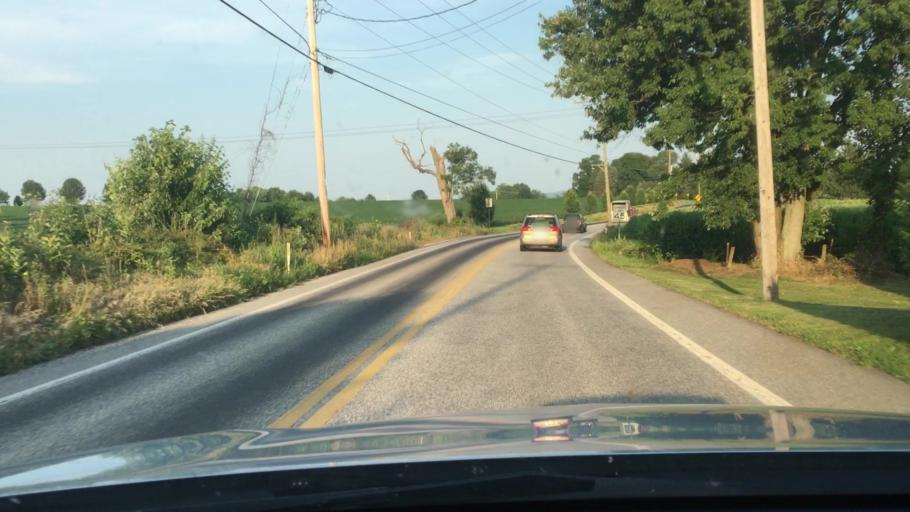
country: US
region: Pennsylvania
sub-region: York County
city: Dillsburg
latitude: 40.1484
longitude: -77.0680
